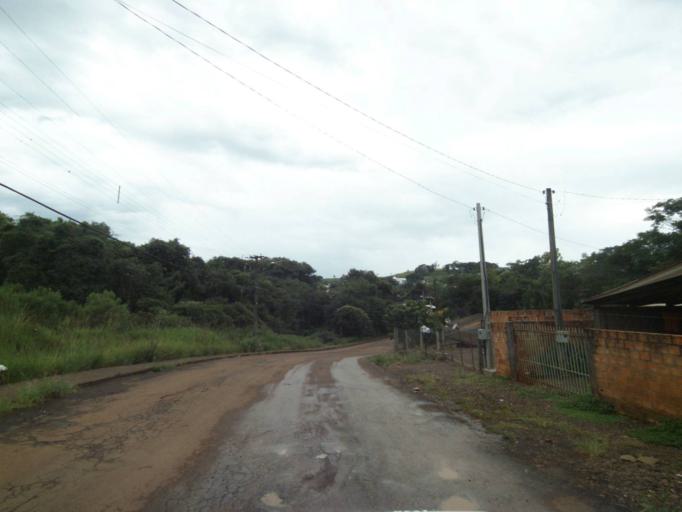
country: BR
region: Parana
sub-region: Guaraniacu
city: Guaraniacu
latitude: -25.1104
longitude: -52.8536
